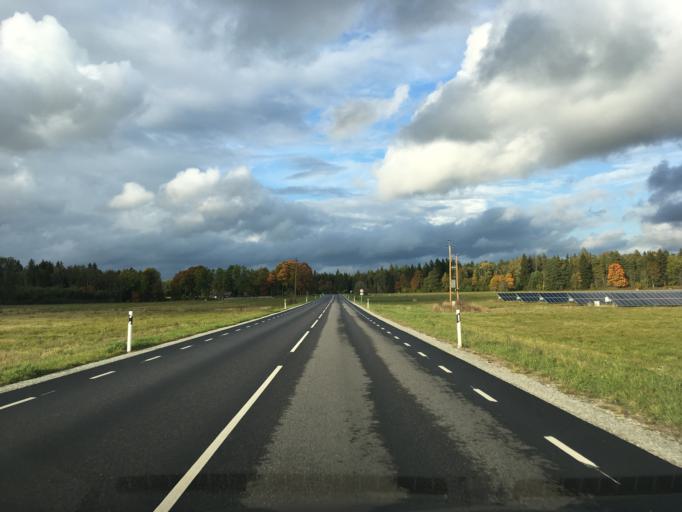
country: EE
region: Harju
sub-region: Paldiski linn
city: Paldiski
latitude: 59.1956
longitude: 24.0950
